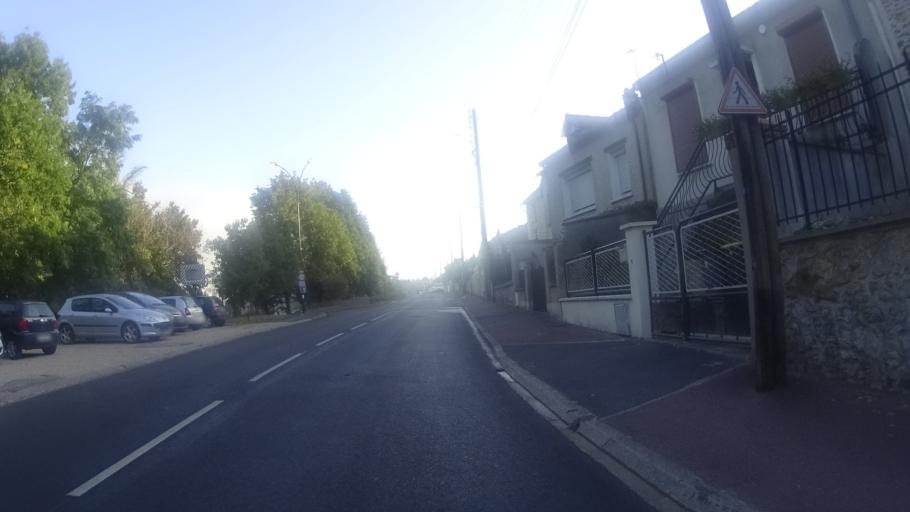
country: FR
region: Ile-de-France
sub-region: Departement de l'Essonne
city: Ormoy
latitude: 48.5814
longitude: 2.4710
